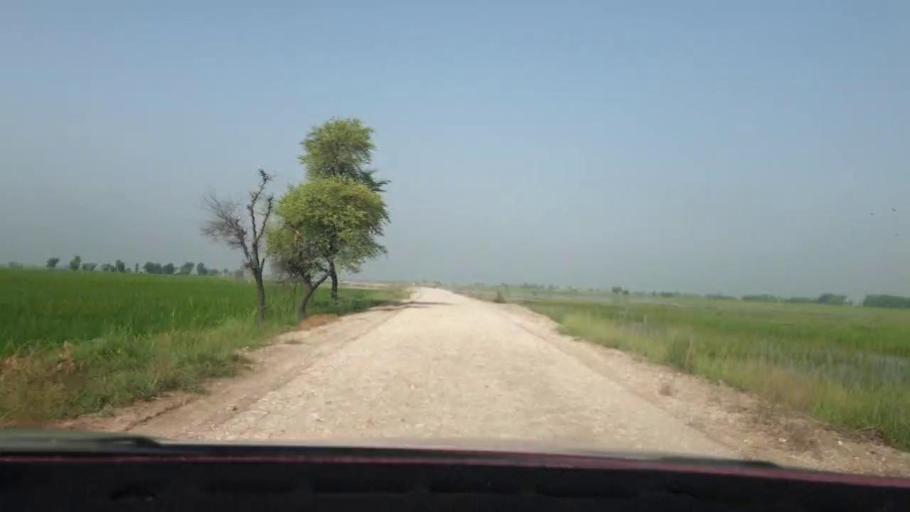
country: PK
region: Sindh
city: Nasirabad
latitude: 27.4385
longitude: 67.9776
